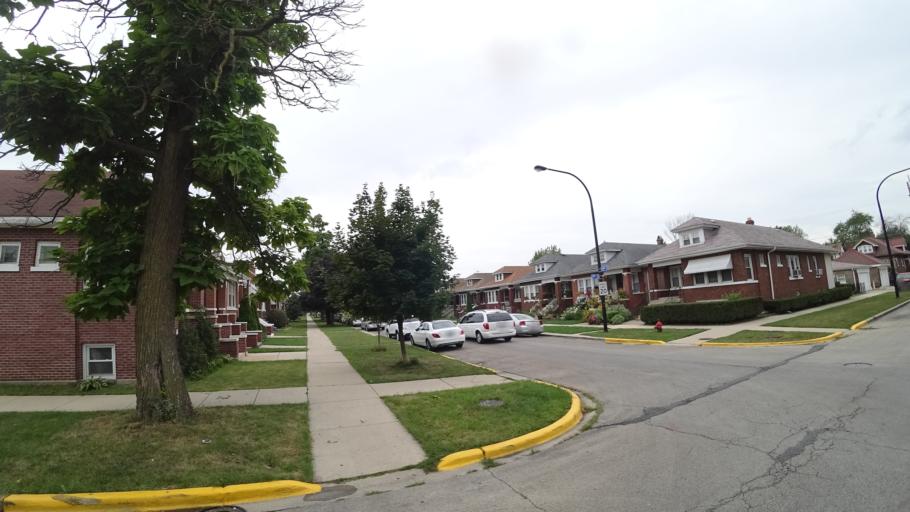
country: US
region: Illinois
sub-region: Cook County
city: Cicero
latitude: 41.8545
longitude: -87.7725
